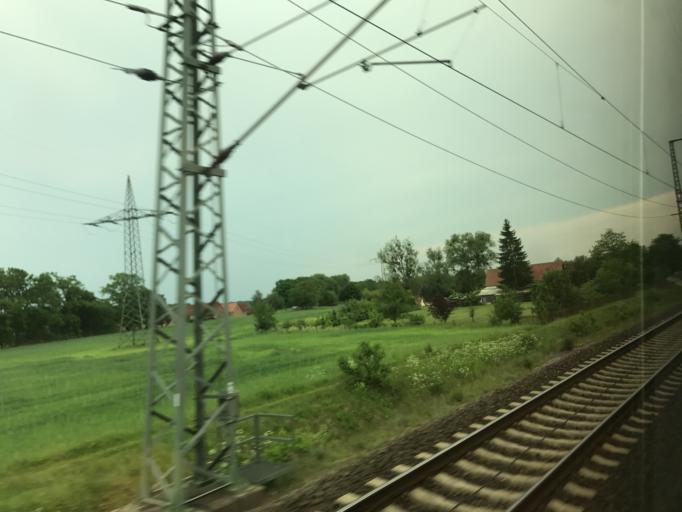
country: DE
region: Saxony-Anhalt
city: Mieste
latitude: 52.5007
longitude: 11.2955
